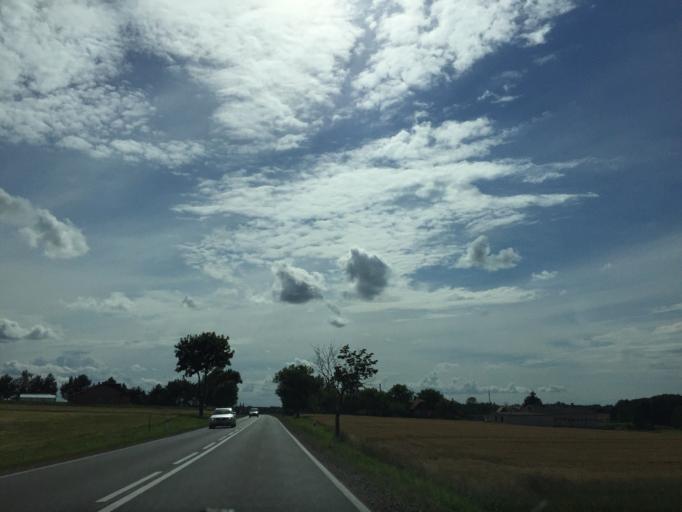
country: PL
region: Masovian Voivodeship
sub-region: Powiat losicki
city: Losice
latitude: 52.2246
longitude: 22.7433
